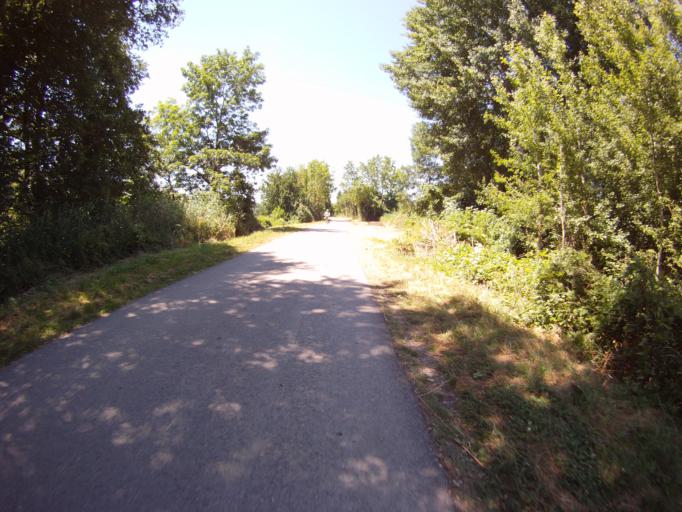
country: FR
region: Champagne-Ardenne
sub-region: Departement de la Marne
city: Damery
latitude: 49.0665
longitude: 3.8874
